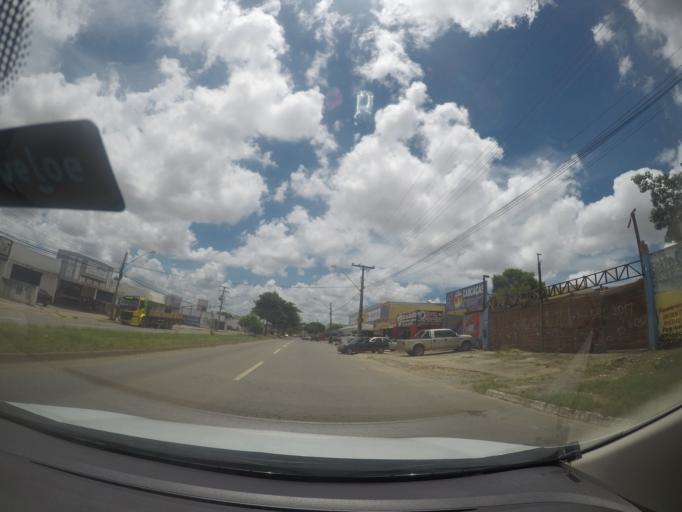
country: BR
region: Goias
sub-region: Goiania
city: Goiania
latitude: -16.6717
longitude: -49.3145
